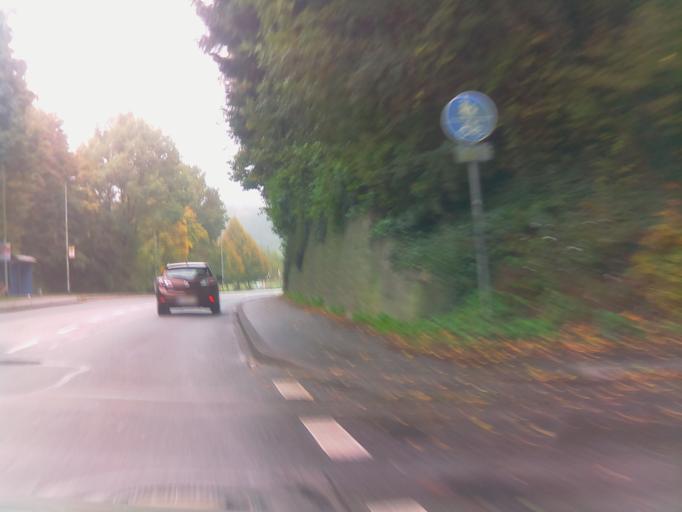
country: DE
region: Baden-Wuerttemberg
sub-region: Karlsruhe Region
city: Bretten
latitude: 49.0274
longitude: 8.7042
